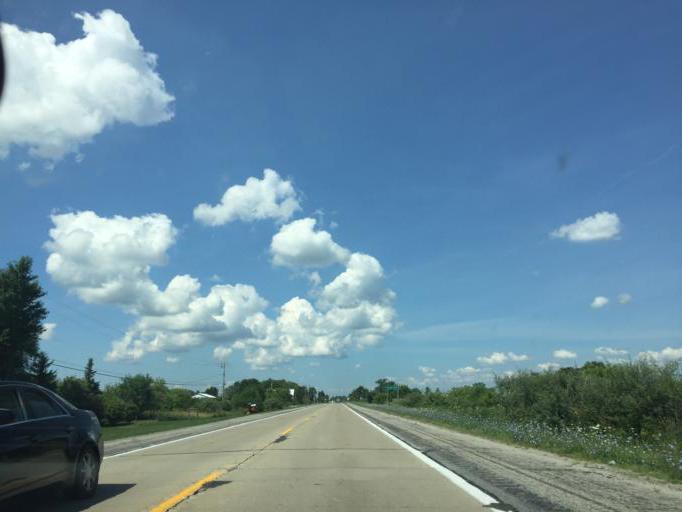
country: US
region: Ohio
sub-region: Lucas County
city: Sylvania
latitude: 41.7965
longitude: -83.7316
